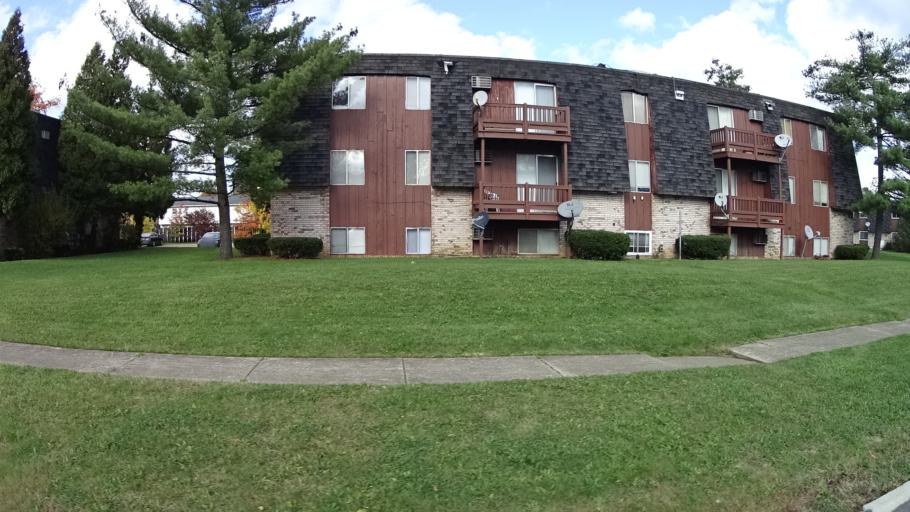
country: US
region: Ohio
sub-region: Lorain County
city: Lorain
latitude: 41.4197
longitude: -82.1903
